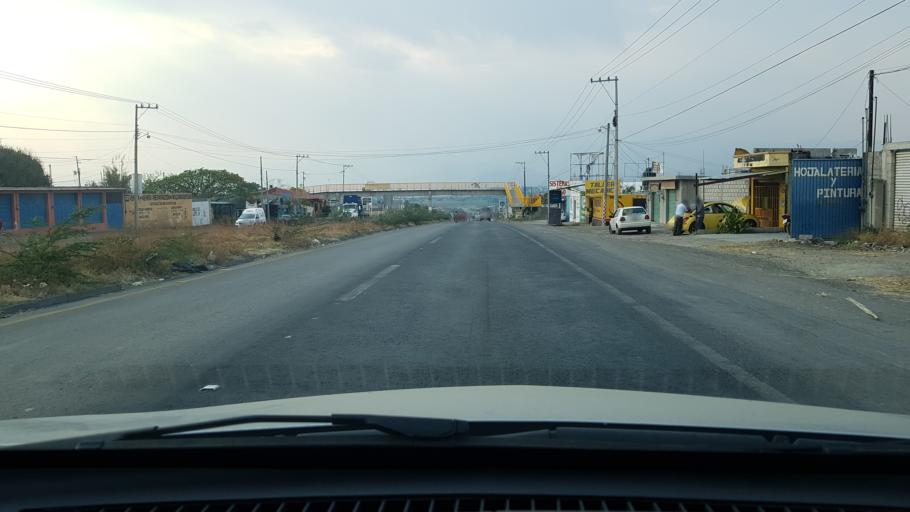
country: MX
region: Morelos
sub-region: Yecapixtla
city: Juan Morales
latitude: 18.8164
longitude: -98.9176
